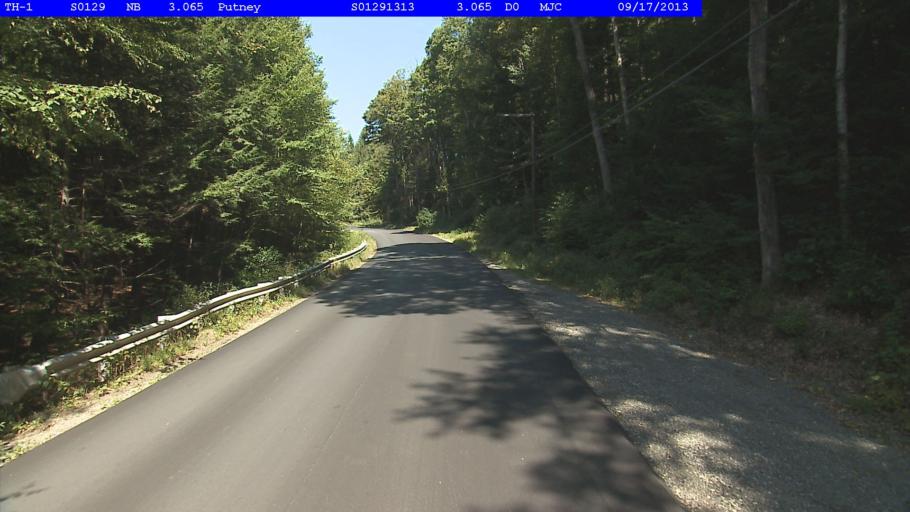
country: US
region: New Hampshire
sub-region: Cheshire County
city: Westmoreland
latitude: 43.0160
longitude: -72.5267
